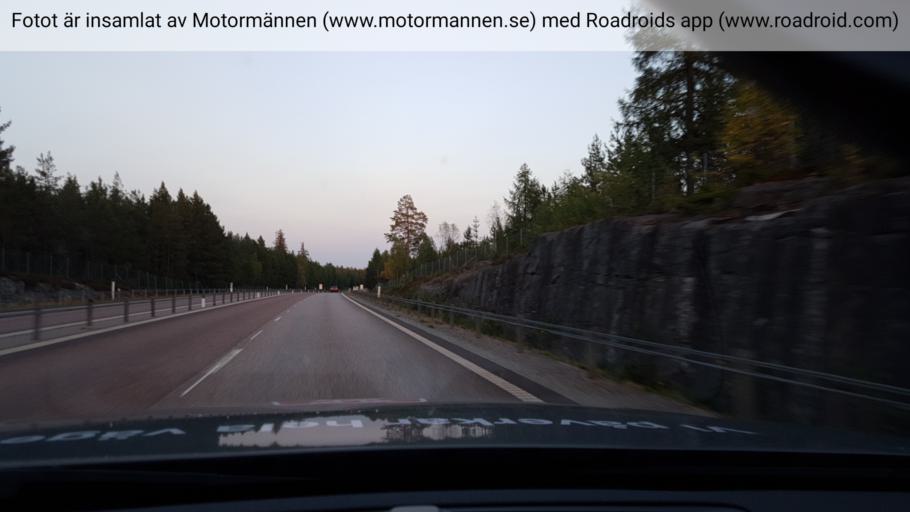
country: SE
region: Vaestmanland
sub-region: Surahammars Kommun
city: Ramnas
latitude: 59.8178
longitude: 16.1199
